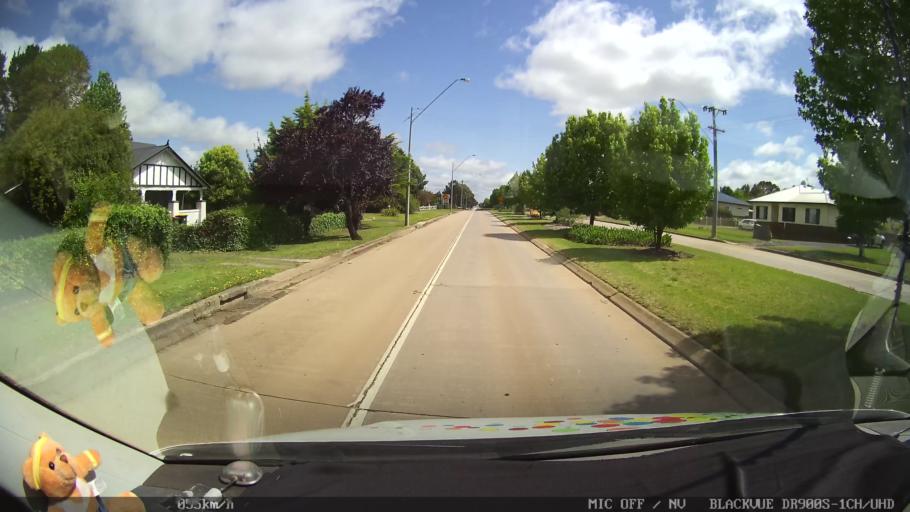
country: AU
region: New South Wales
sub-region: Glen Innes Severn
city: Glen Innes
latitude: -29.7493
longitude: 151.7361
